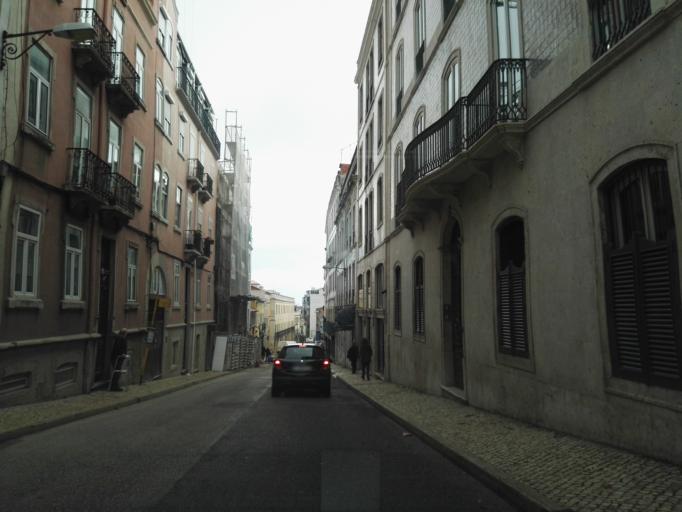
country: PT
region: Lisbon
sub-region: Lisbon
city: Lisbon
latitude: 38.7179
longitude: -9.1554
